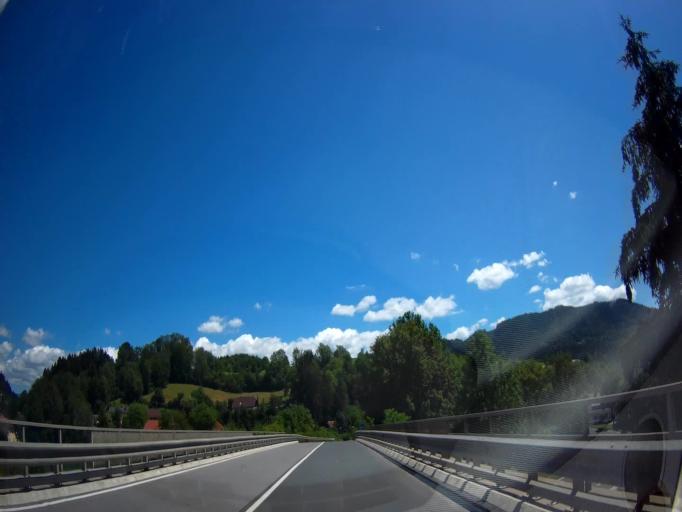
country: AT
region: Carinthia
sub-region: Politischer Bezirk Sankt Veit an der Glan
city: Sankt Veit an der Glan
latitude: 46.7461
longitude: 14.3866
